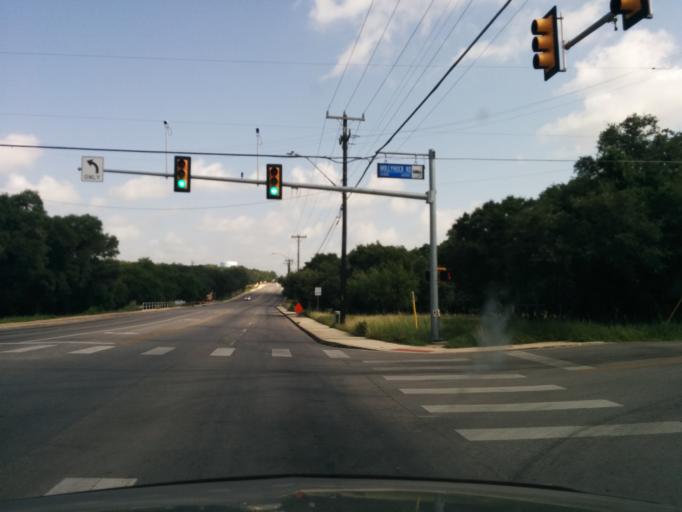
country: US
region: Texas
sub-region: Bexar County
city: Leon Valley
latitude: 29.5338
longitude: -98.6061
